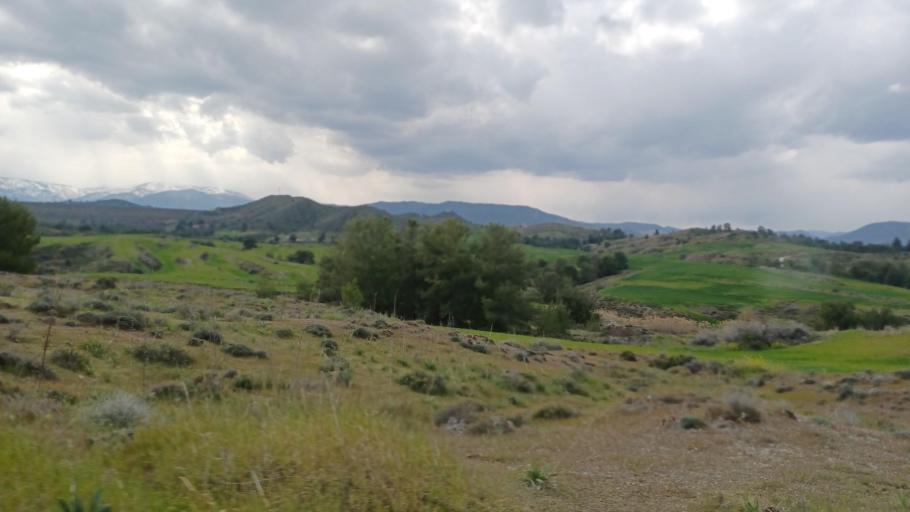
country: CY
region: Lefkosia
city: Lefka
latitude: 35.0820
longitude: 32.9051
